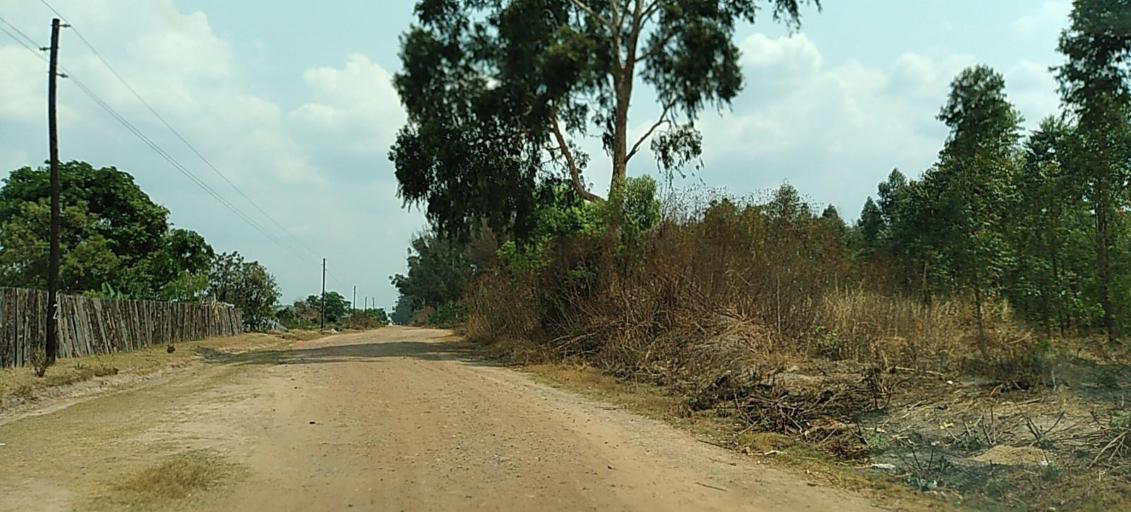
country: ZM
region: Copperbelt
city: Kalulushi
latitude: -12.8379
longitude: 28.0776
